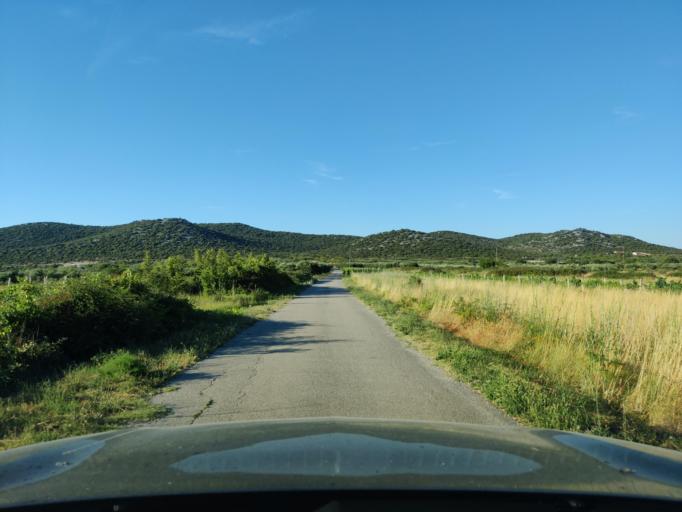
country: HR
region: Sibensko-Kniniska
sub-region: Grad Sibenik
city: Pirovac
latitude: 43.8614
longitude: 15.6951
